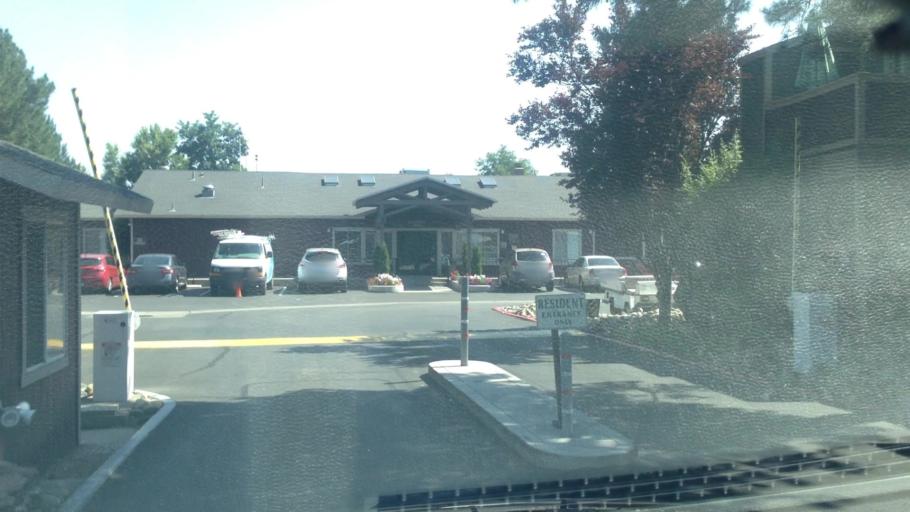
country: US
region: Nevada
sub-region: Washoe County
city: Sparks
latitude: 39.4858
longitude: -119.7446
